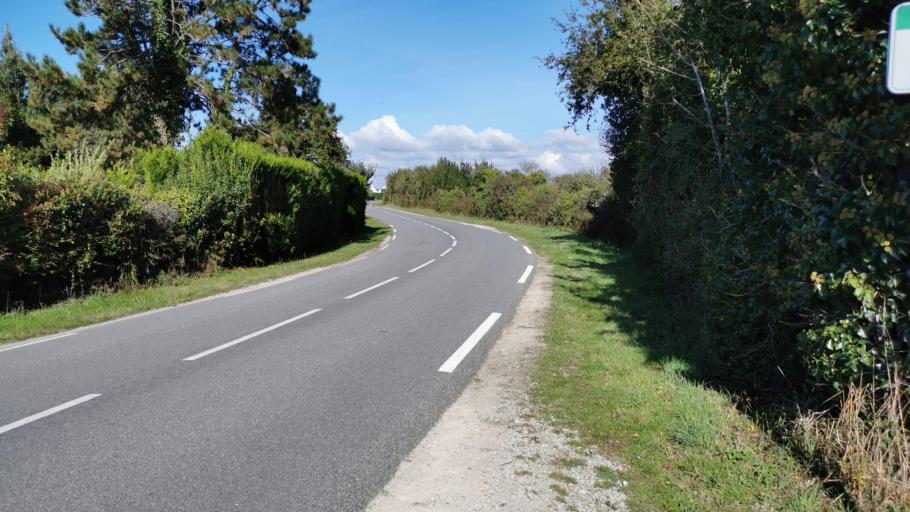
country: FR
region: Brittany
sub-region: Departement du Morbihan
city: Arzon
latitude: 47.5486
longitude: -2.8765
